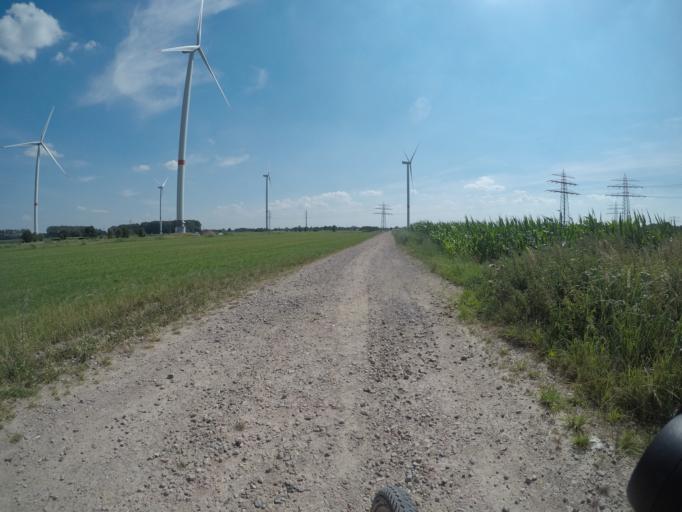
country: DE
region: Hamburg
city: Bergedorf
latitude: 53.4758
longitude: 10.2127
